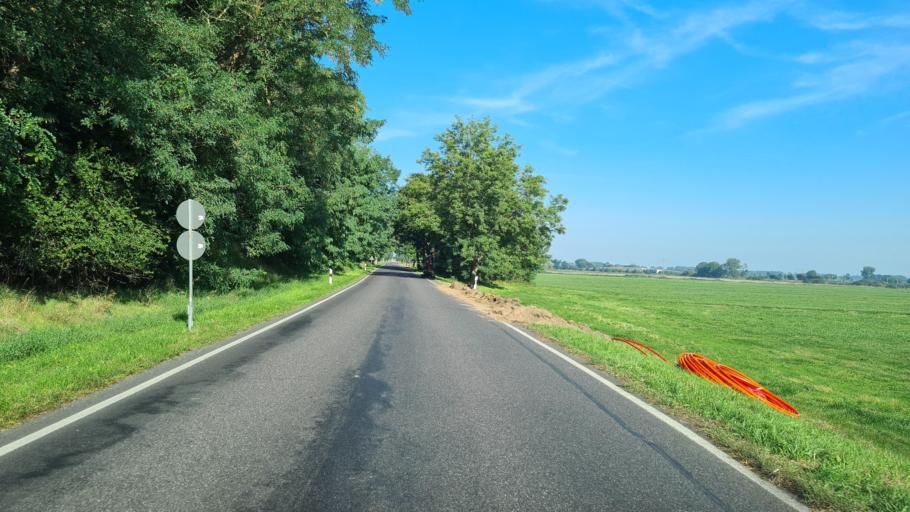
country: DE
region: Brandenburg
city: Friesack
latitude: 52.7182
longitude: 12.6381
